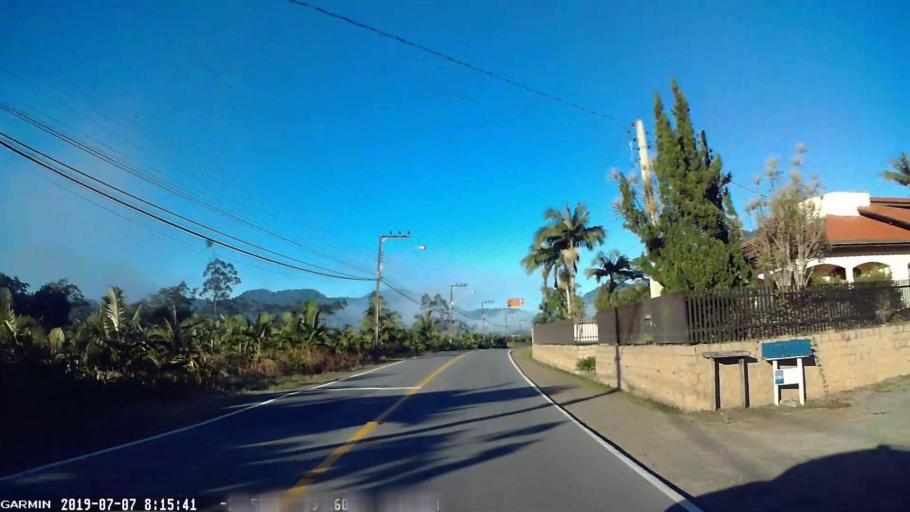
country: BR
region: Santa Catarina
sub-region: Jaragua Do Sul
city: Jaragua do Sul
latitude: -26.5503
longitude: -49.1604
